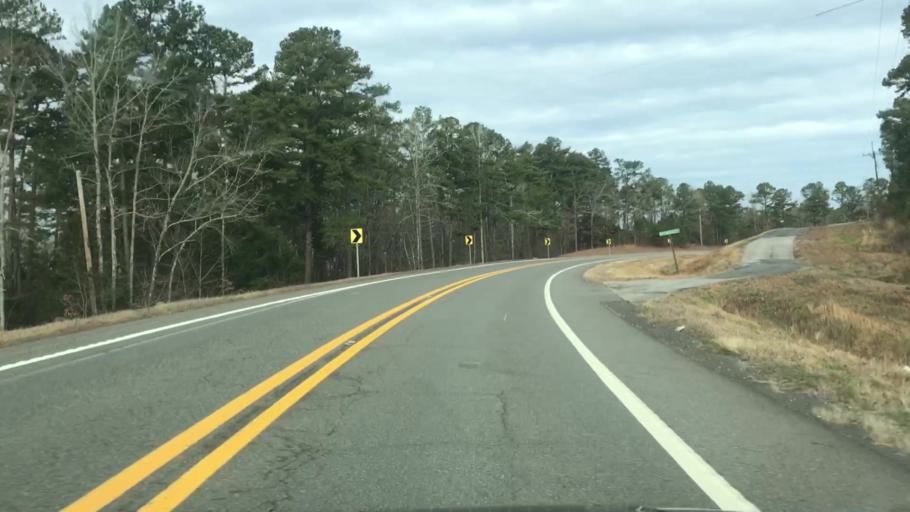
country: US
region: Arkansas
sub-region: Montgomery County
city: Mount Ida
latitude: 34.6122
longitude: -93.7026
